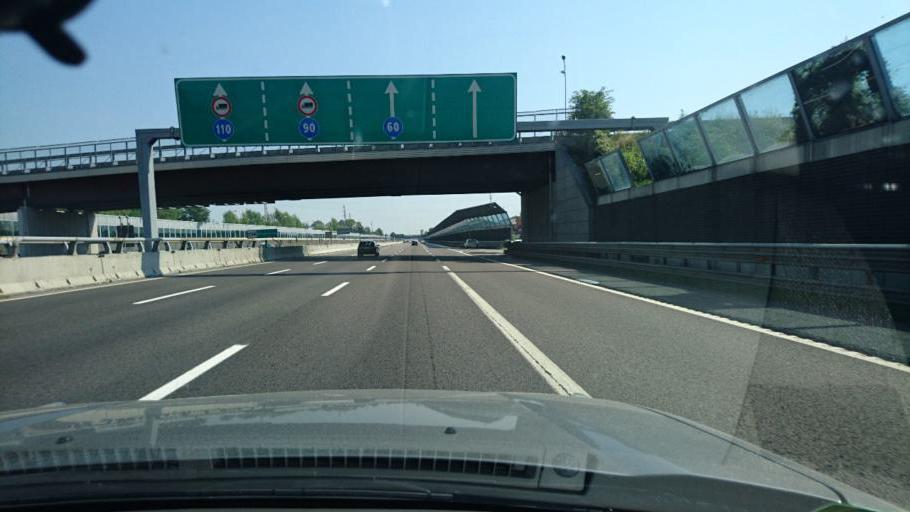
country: IT
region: Lombardy
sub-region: Provincia di Monza e Brianza
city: Monza
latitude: 45.5570
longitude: 9.2756
